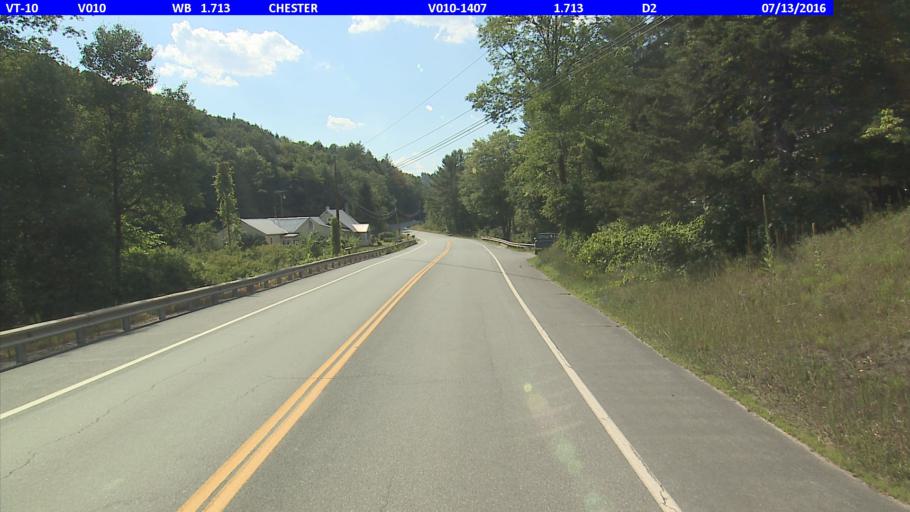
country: US
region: Vermont
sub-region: Windsor County
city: Chester
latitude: 43.3260
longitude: -72.5744
